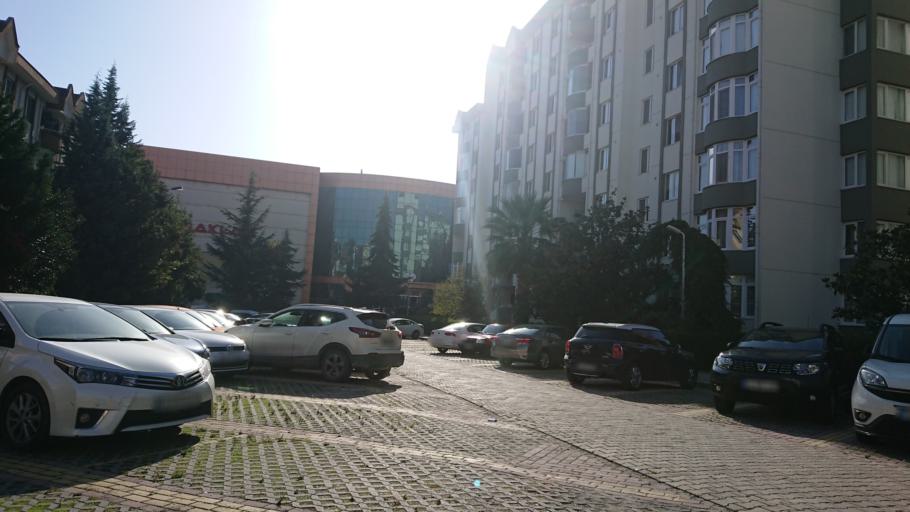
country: TR
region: Istanbul
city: Esenyurt
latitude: 41.0619
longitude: 28.6768
